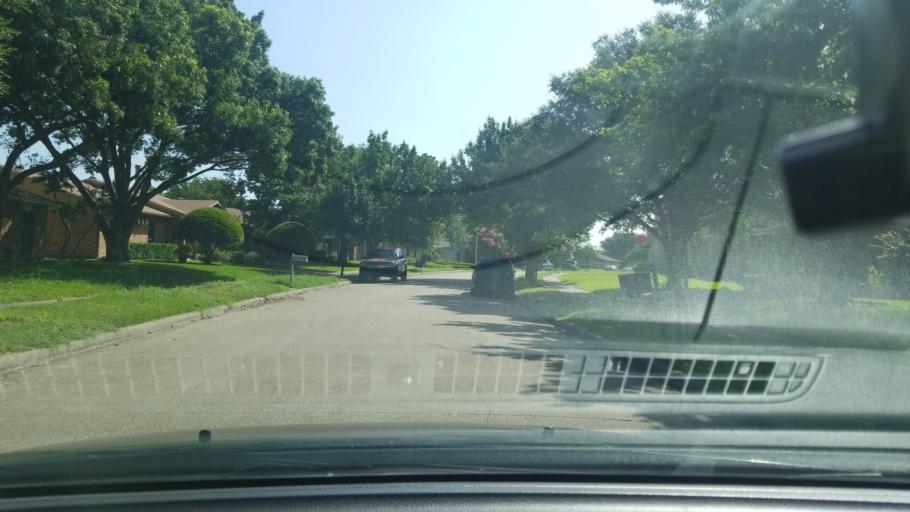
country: US
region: Texas
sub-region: Dallas County
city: Mesquite
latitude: 32.8031
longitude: -96.6937
